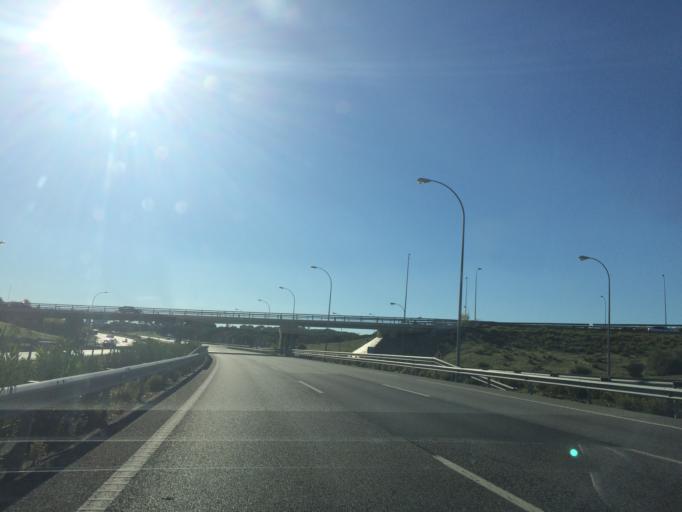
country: ES
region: Madrid
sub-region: Provincia de Madrid
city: Pozuelo de Alarcon
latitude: 40.4593
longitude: -3.8119
